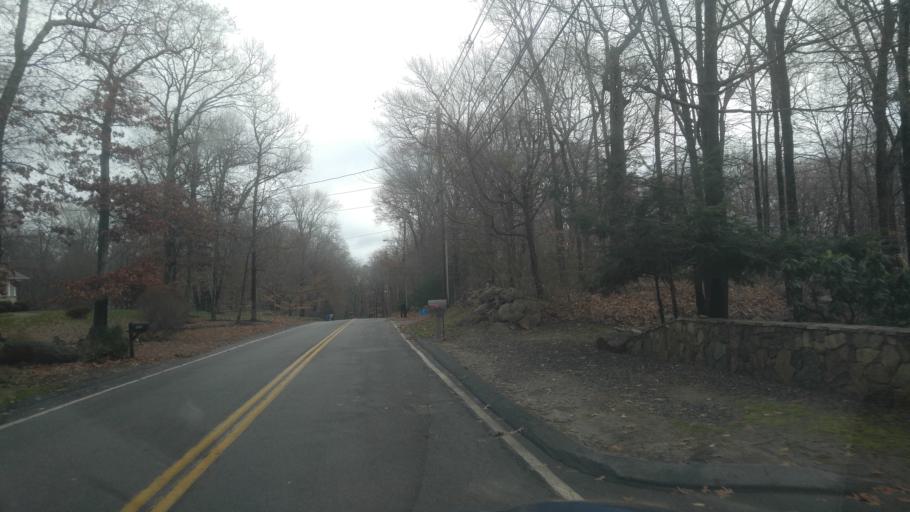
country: US
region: Rhode Island
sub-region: Kent County
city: West Warwick
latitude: 41.6421
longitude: -71.5404
